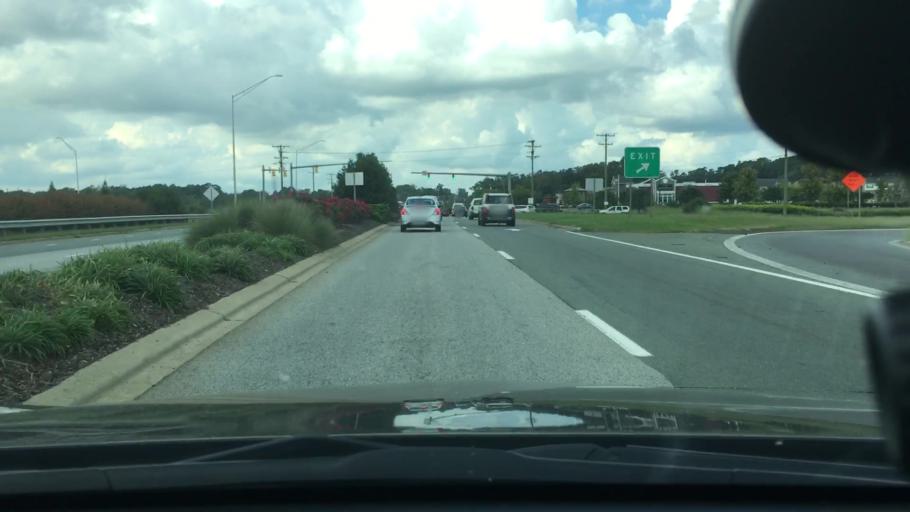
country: US
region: North Carolina
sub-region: Alamance County
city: Elon
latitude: 36.0658
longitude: -79.5163
